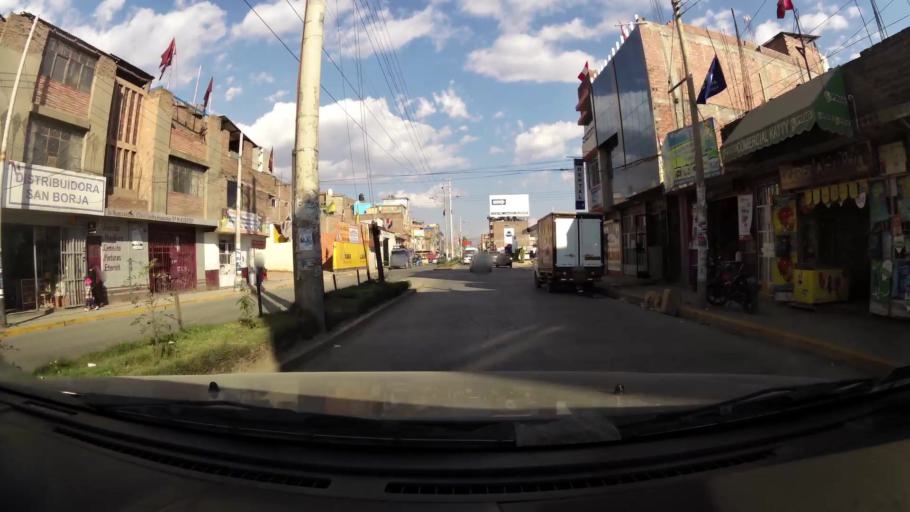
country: PE
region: Junin
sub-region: Provincia de Huancayo
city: El Tambo
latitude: -12.0557
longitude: -75.2237
